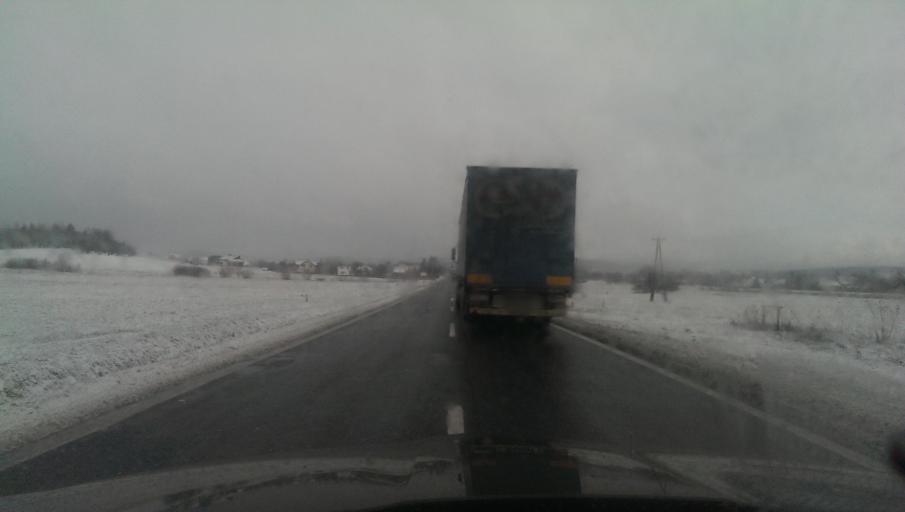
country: PL
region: Subcarpathian Voivodeship
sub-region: Powiat sanocki
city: Strachocina
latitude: 49.5661
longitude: 22.1349
